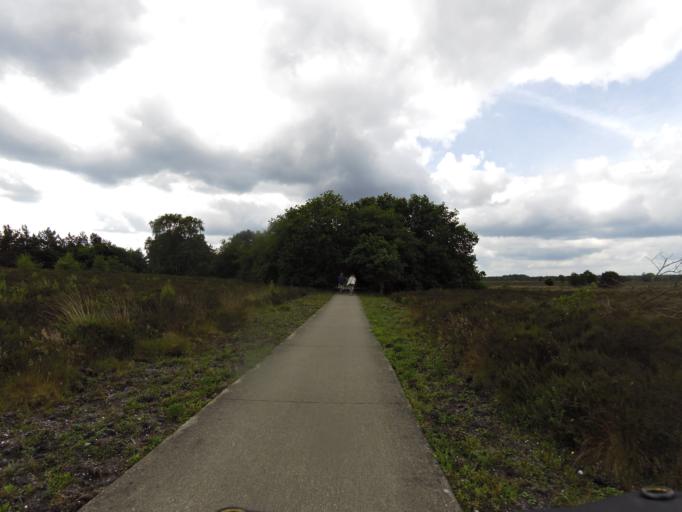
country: NL
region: Gelderland
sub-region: Gemeente Apeldoorn
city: Uddel
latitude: 52.3131
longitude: 5.8128
